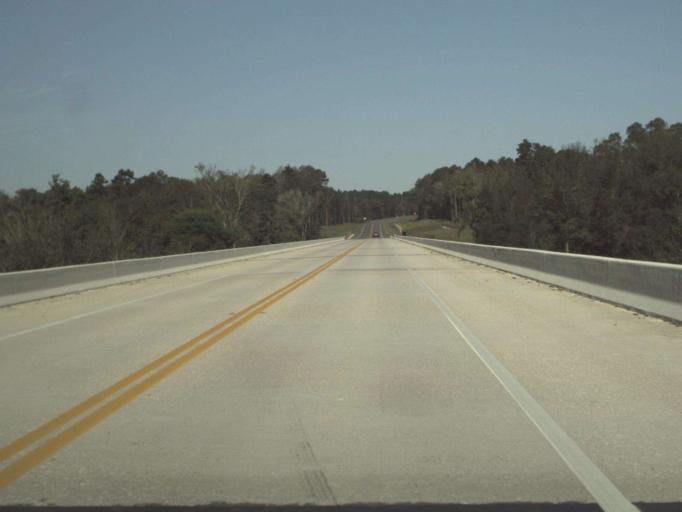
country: US
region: Florida
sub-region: Gadsden County
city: Quincy
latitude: 30.5844
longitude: -84.5507
